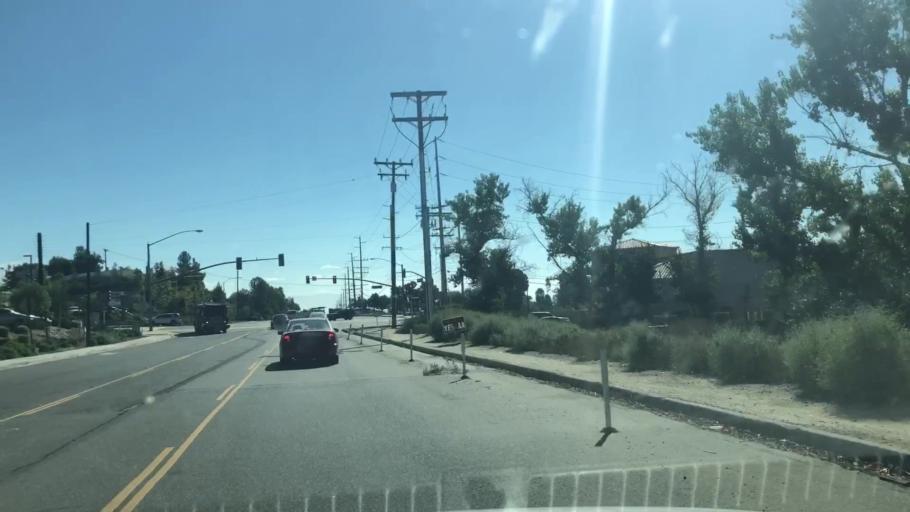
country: US
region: California
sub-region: Riverside County
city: Wildomar
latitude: 33.5899
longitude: -117.2531
